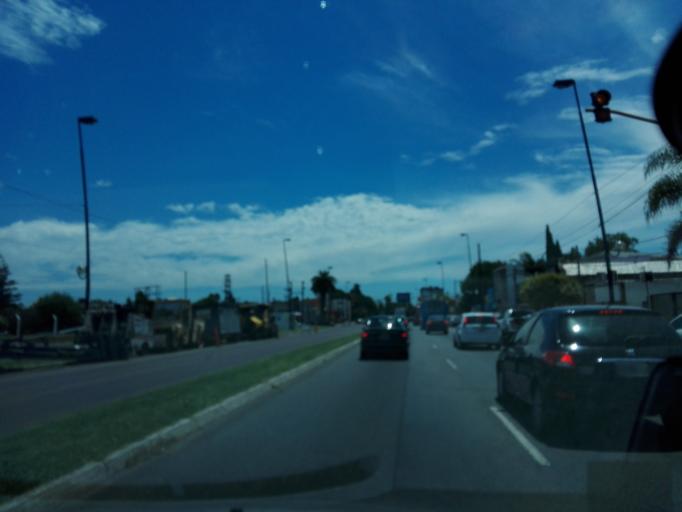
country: AR
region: Buenos Aires
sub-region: Partido de La Plata
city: La Plata
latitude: -34.8841
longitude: -58.0047
